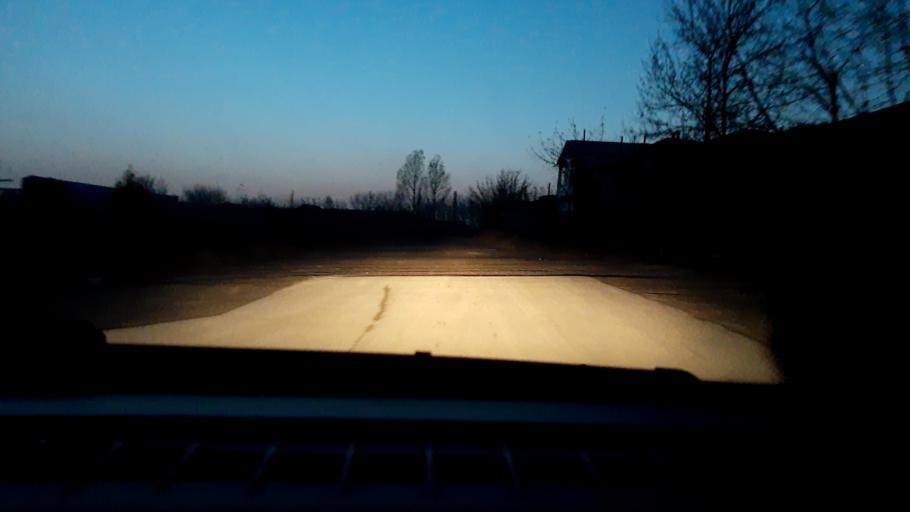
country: RU
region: Nizjnij Novgorod
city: Nizhniy Novgorod
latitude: 56.2650
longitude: 43.9554
